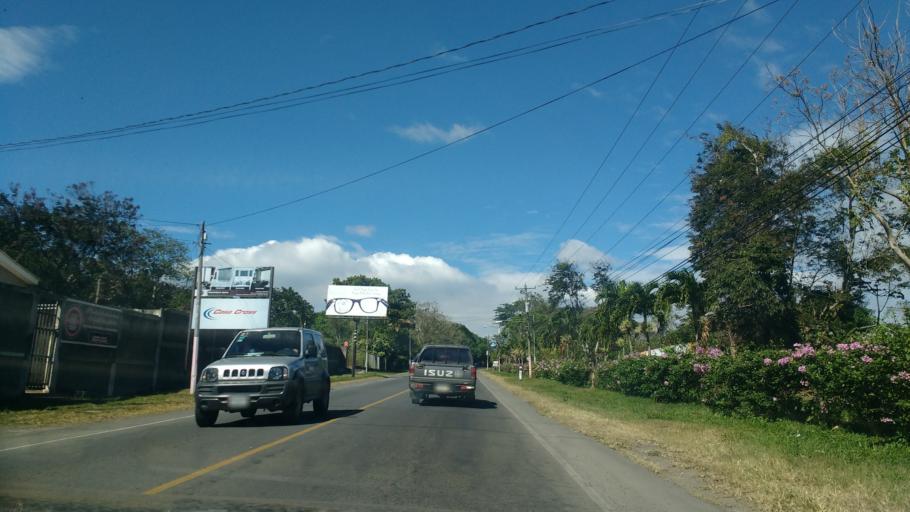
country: NI
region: Carazo
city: Diriamba
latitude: 11.8712
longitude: -86.2388
